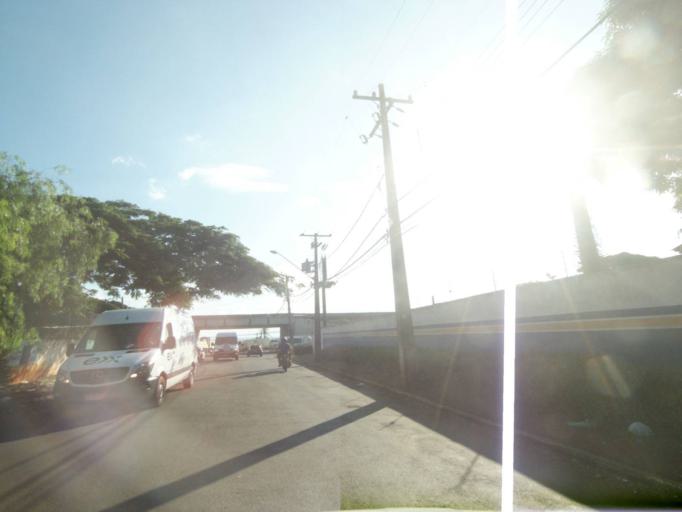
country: BR
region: Parana
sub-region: Londrina
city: Londrina
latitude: -23.3037
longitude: -51.2234
